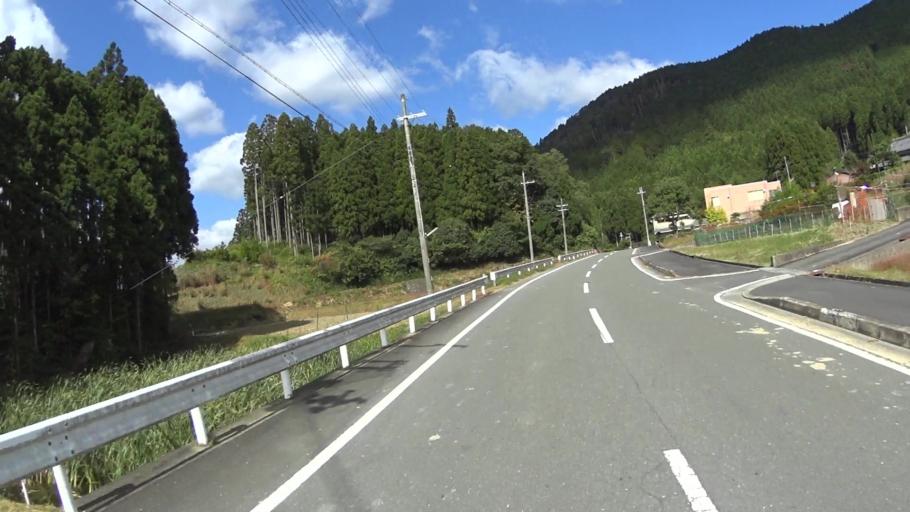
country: JP
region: Kyoto
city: Kameoka
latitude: 35.1119
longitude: 135.5728
